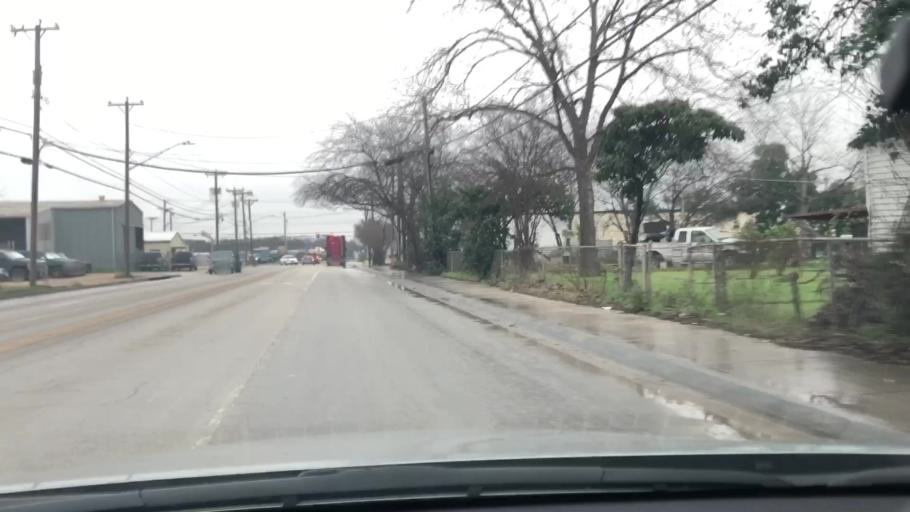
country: US
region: Texas
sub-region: Bexar County
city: Kirby
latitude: 29.4355
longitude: -98.4075
